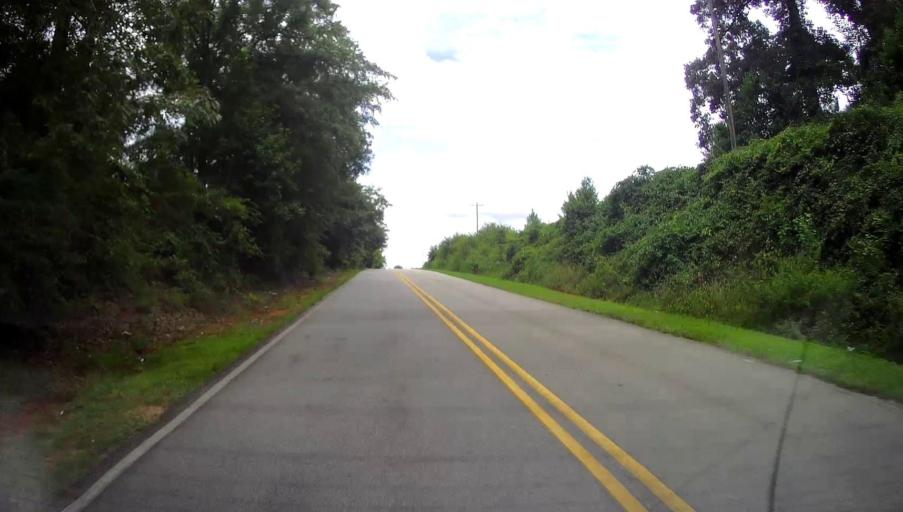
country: US
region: Georgia
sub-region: Houston County
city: Perry
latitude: 32.5544
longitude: -83.7534
